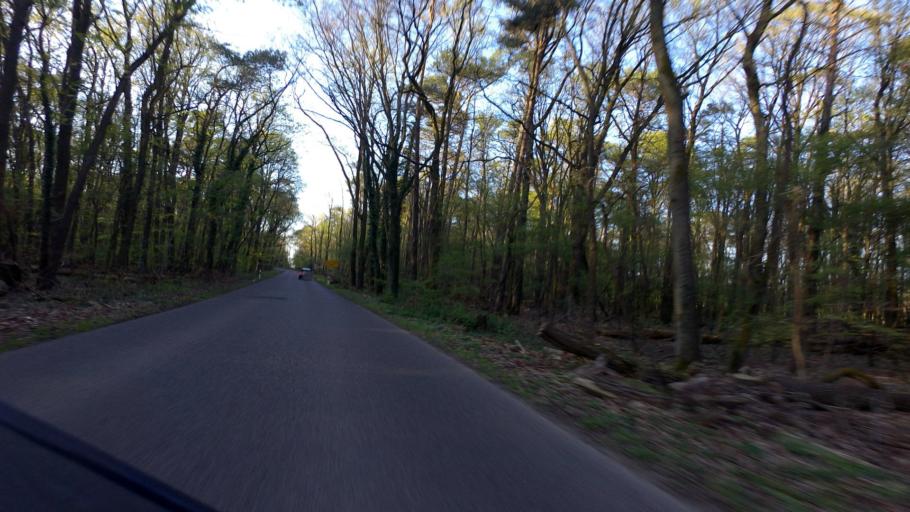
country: DE
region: Berlin
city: Kladow
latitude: 52.4935
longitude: 13.1245
